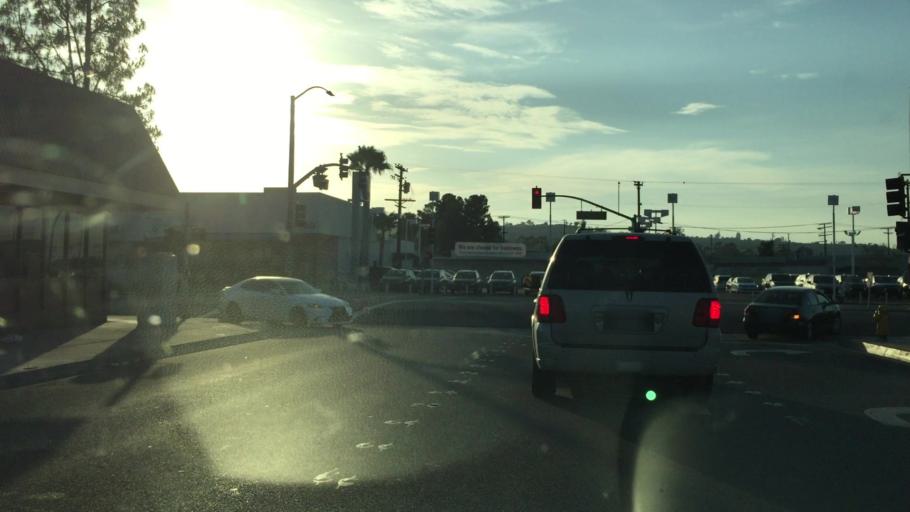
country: US
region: California
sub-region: San Diego County
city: El Cajon
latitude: 32.7926
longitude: -116.9695
